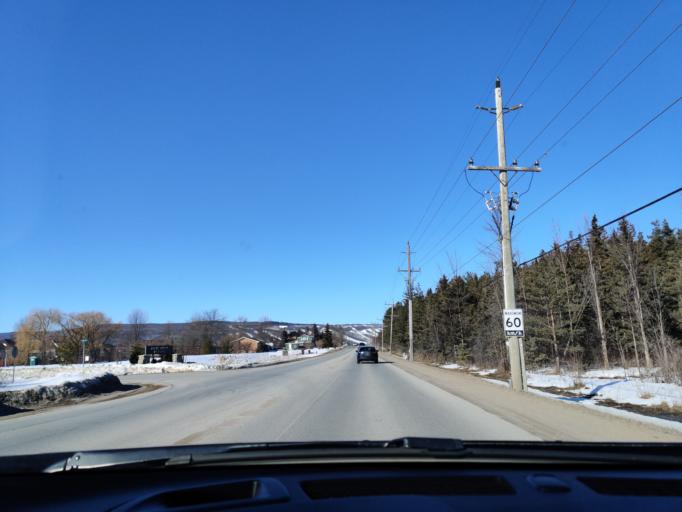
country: CA
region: Ontario
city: Collingwood
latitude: 44.4987
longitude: -80.2626
